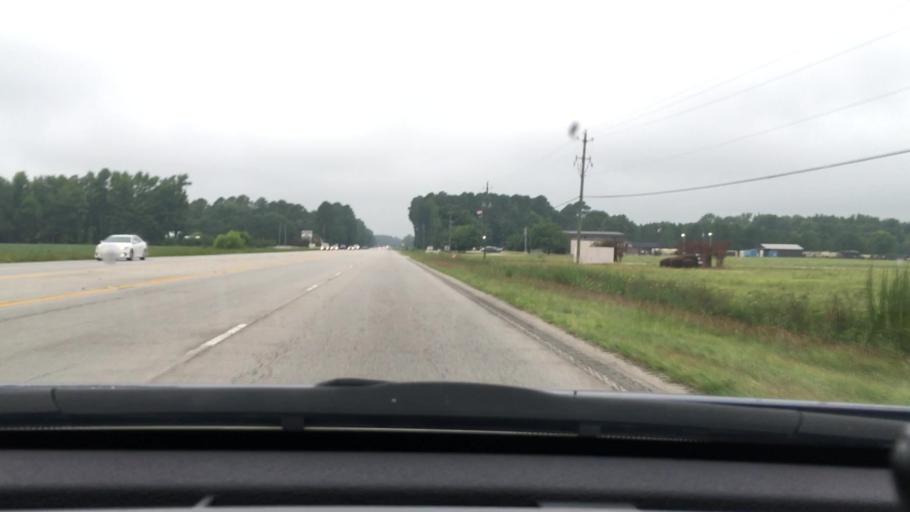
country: US
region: South Carolina
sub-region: Darlington County
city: Darlington
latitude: 34.2997
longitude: -79.9333
